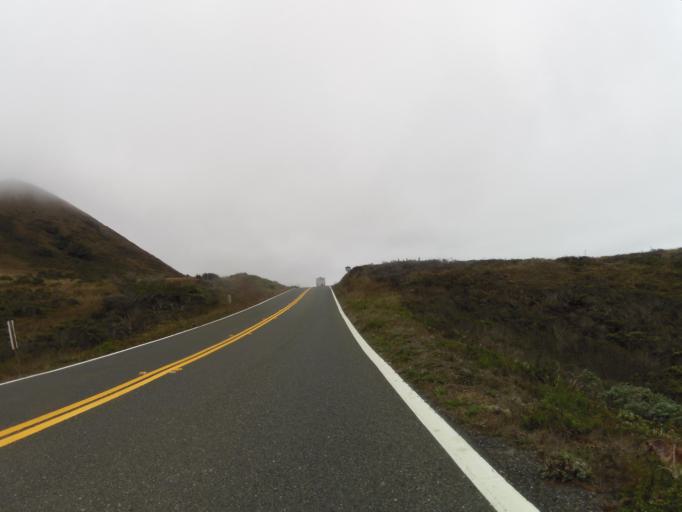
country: US
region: California
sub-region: Sonoma County
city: Monte Rio
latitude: 38.4640
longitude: -123.1501
